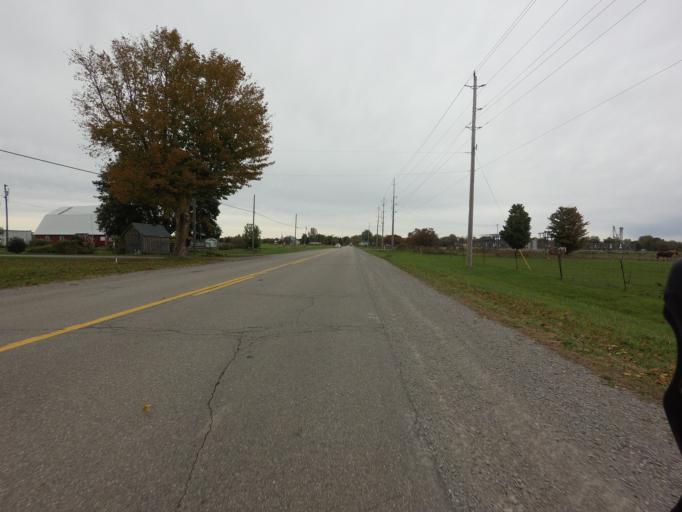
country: CA
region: Ontario
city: Brockville
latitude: 44.6581
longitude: -75.8874
